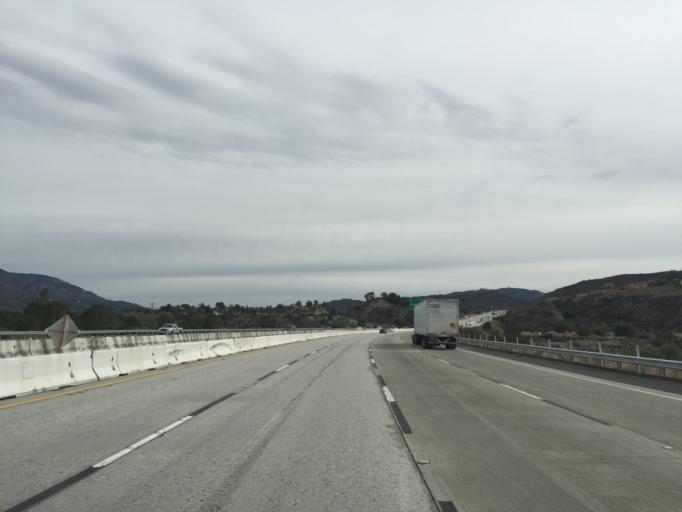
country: US
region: California
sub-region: Los Angeles County
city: Burbank
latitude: 34.2694
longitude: -118.3401
